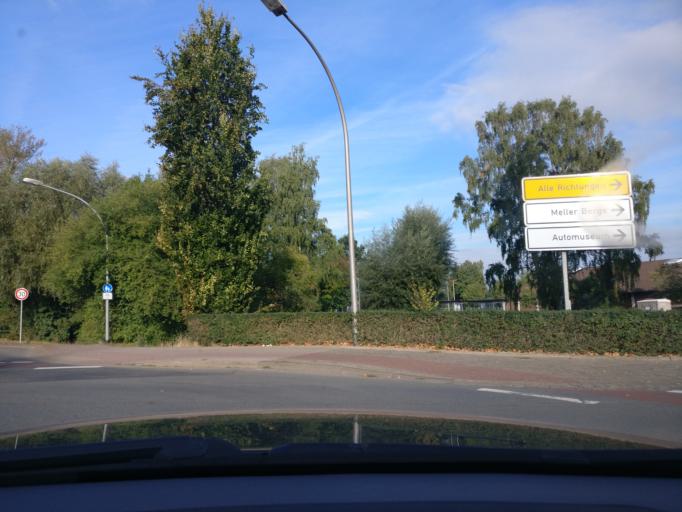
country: DE
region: Lower Saxony
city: Melle
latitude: 52.2050
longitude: 8.3362
